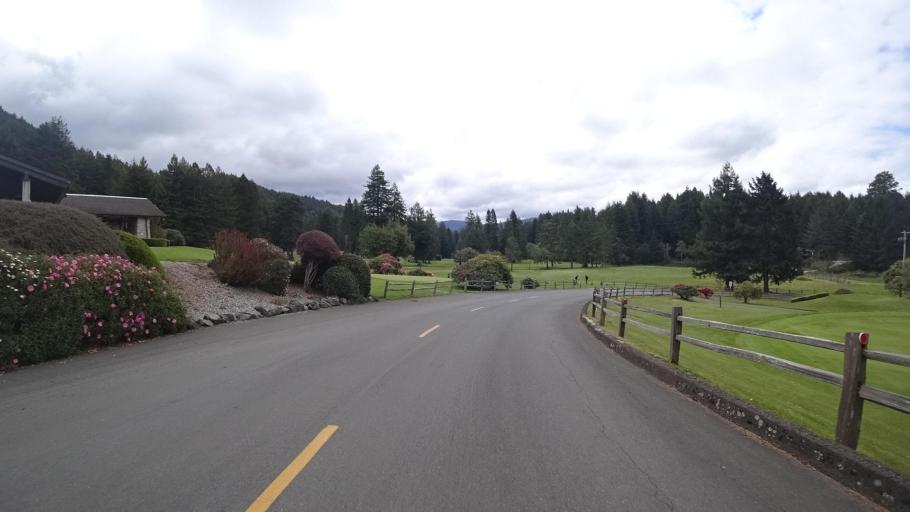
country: US
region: California
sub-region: Humboldt County
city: Bayside
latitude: 40.8468
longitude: -124.0483
